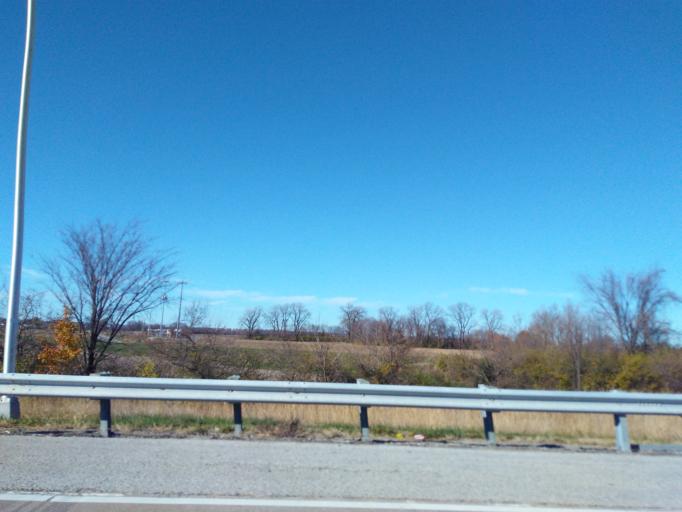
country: US
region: Illinois
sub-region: Saint Clair County
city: Dupo
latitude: 38.4803
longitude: -90.2231
